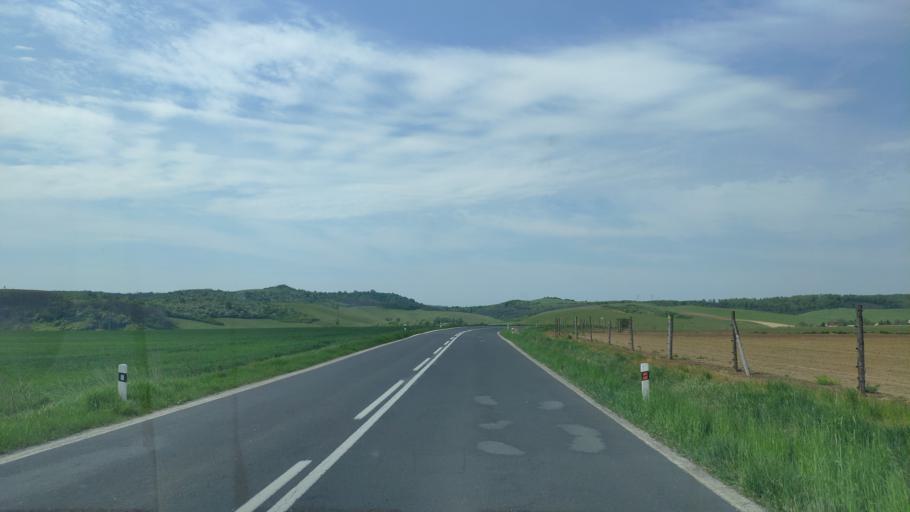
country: HU
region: Borsod-Abauj-Zemplen
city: Ozd
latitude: 48.4010
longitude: 20.2721
